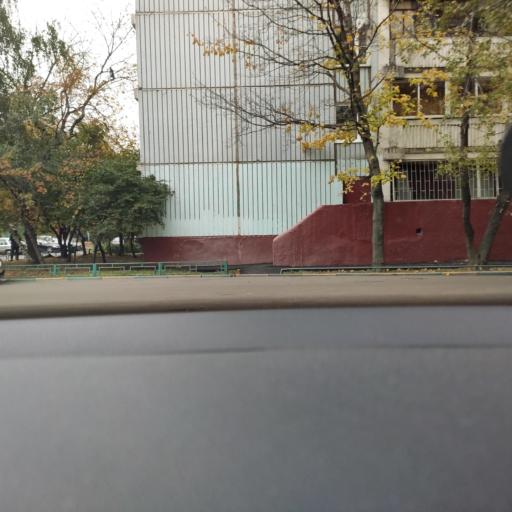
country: RU
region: Moscow
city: Kozeyevo
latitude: 55.8580
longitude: 37.6148
